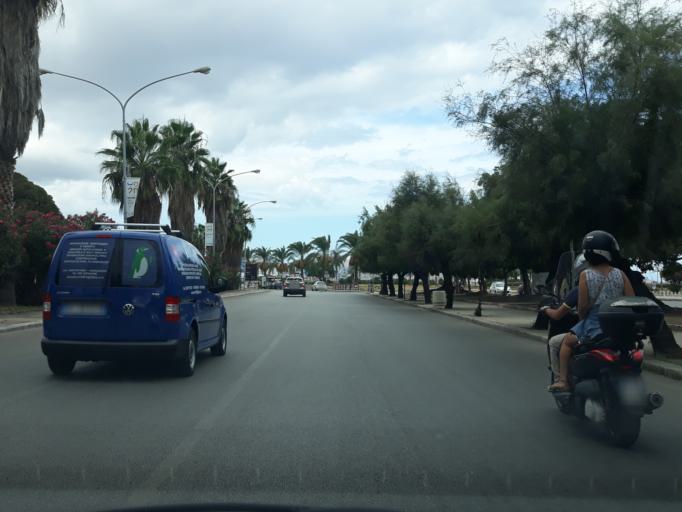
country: IT
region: Sicily
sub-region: Palermo
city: Palermo
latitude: 38.1144
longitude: 13.3770
